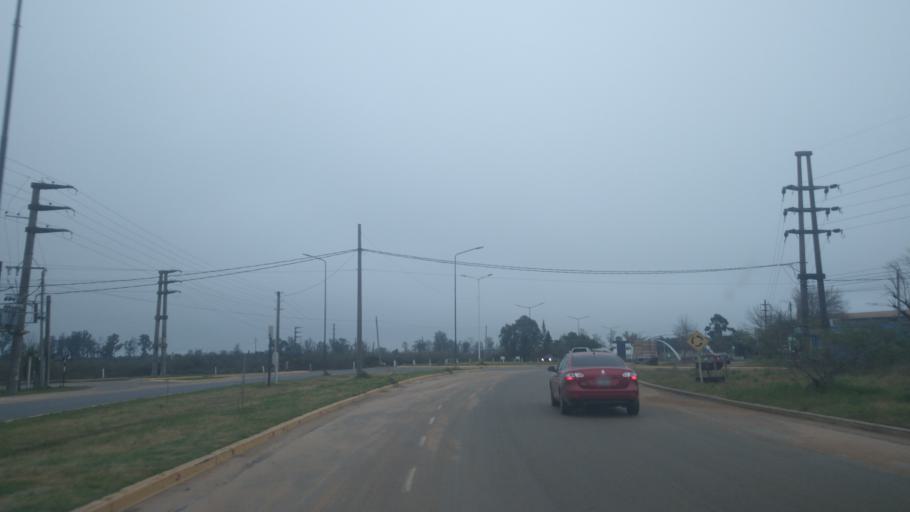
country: AR
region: Entre Rios
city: Chajari
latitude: -30.7624
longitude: -58.0140
